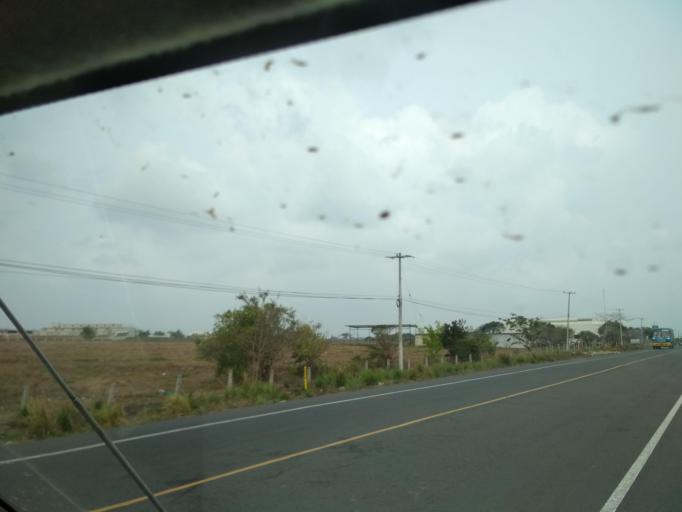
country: MX
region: Veracruz
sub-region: Medellin
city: La Laguna y Monte del Castillo
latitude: 19.0023
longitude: -96.1077
